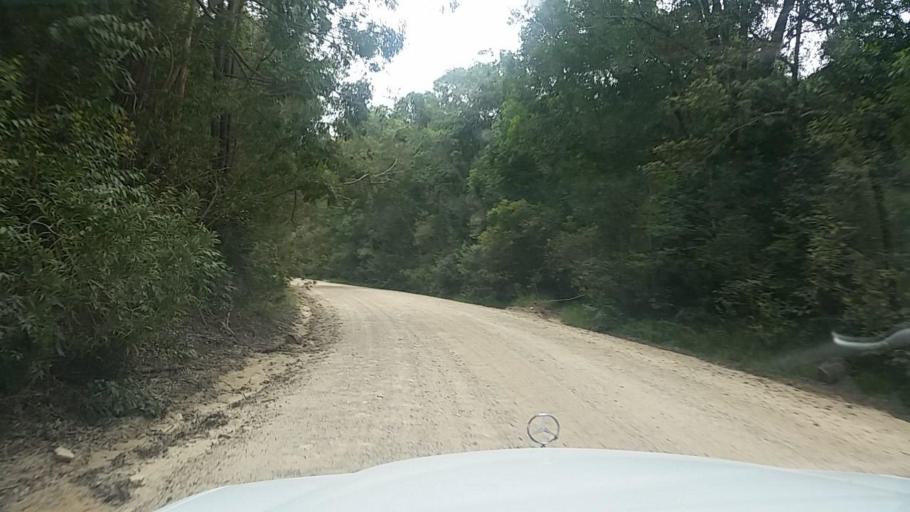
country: ZA
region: Western Cape
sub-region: Eden District Municipality
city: Knysna
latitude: -33.9956
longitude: 23.1181
